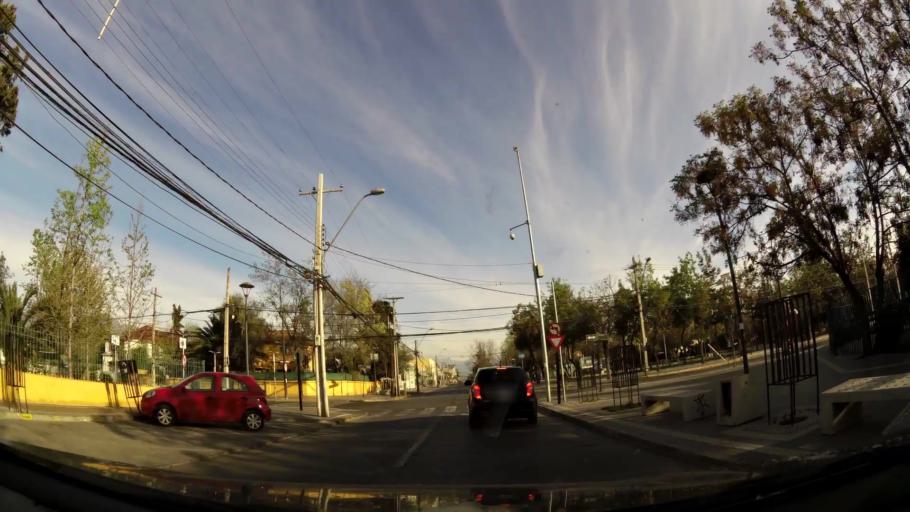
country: CL
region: Santiago Metropolitan
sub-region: Provincia de Cordillera
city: Puente Alto
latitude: -33.6072
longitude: -70.5781
